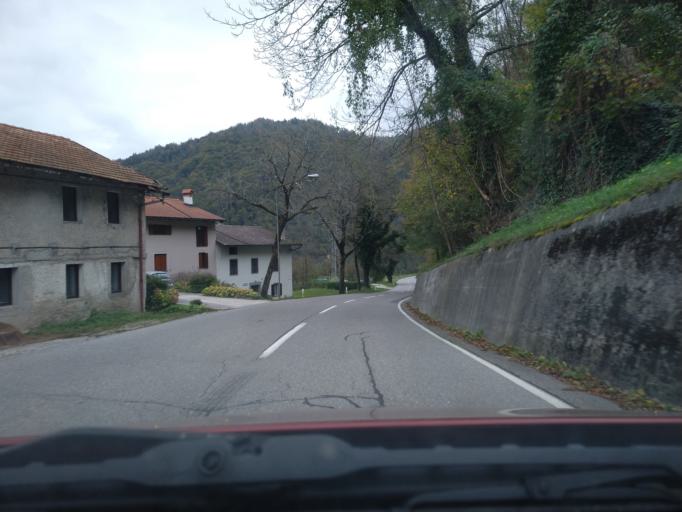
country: SI
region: Tolmin
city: Tolmin
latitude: 46.1620
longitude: 13.7111
